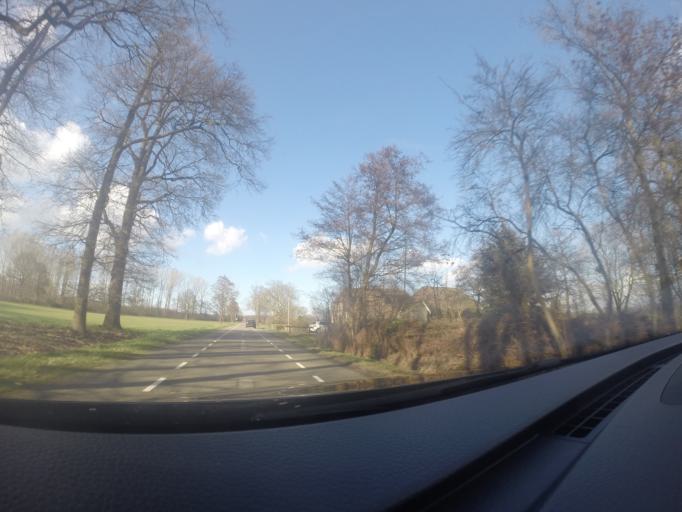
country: NL
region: Gelderland
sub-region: Gemeente Lochem
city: Barchem
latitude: 52.0440
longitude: 6.4475
